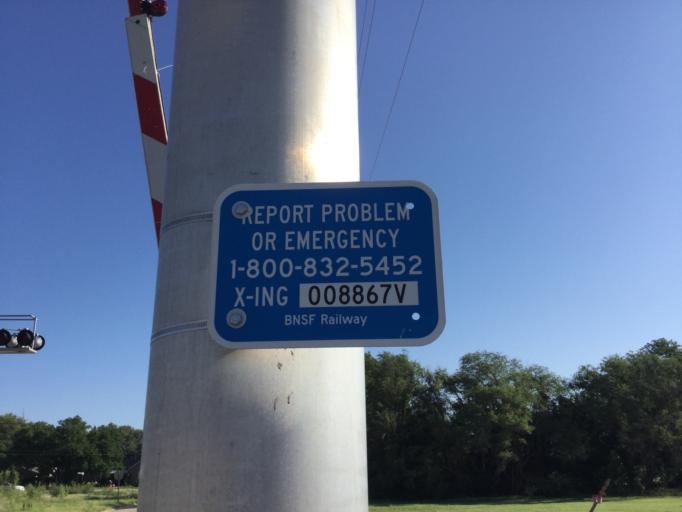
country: US
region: Kansas
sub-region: Reno County
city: Buhler
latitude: 38.0242
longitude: -97.6755
